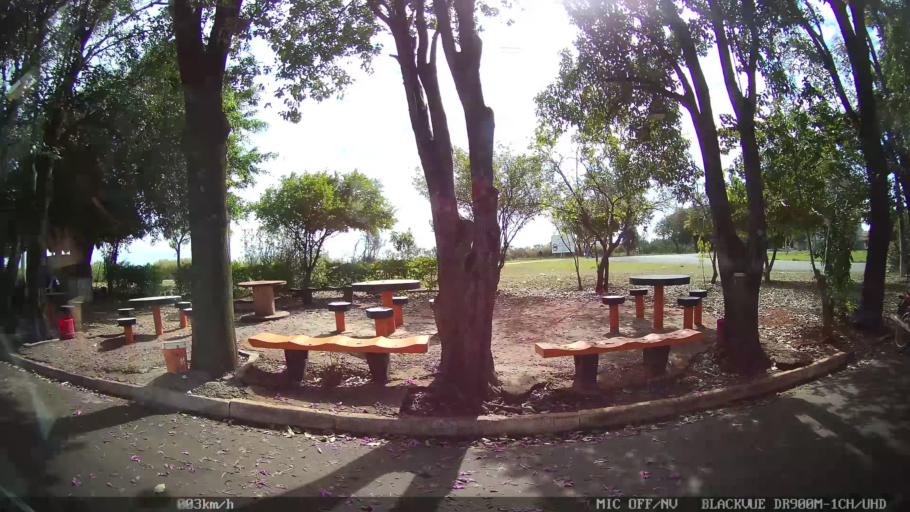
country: BR
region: Sao Paulo
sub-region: Santa Barbara D'Oeste
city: Santa Barbara d'Oeste
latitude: -22.7500
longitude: -47.4278
